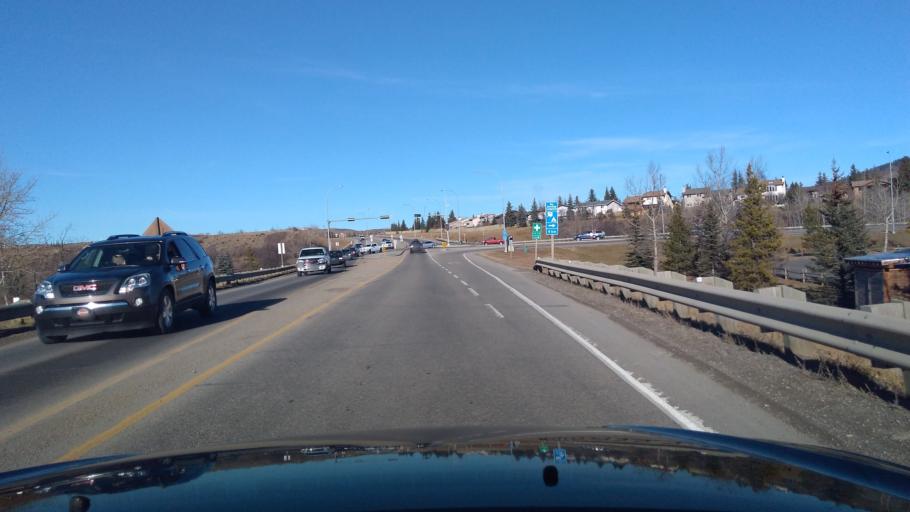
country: CA
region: Alberta
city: Cochrane
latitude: 51.1838
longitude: -114.4872
